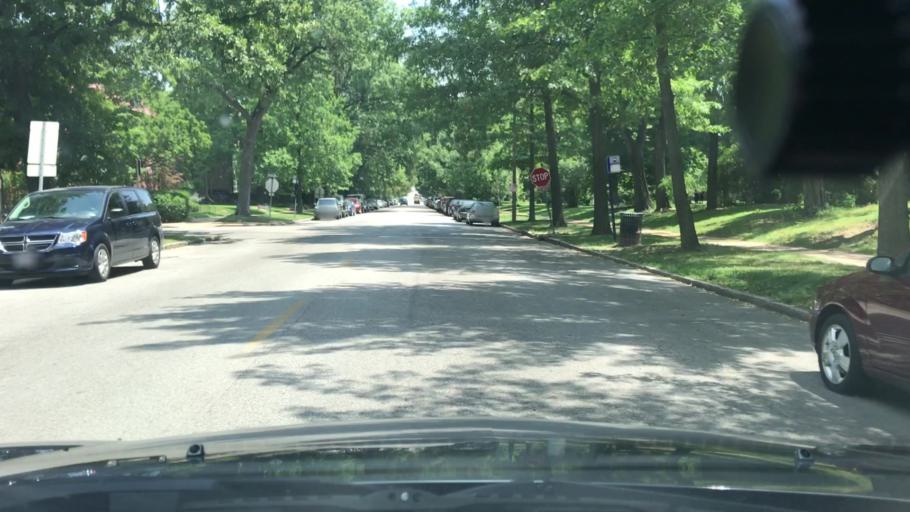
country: US
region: Missouri
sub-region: City of Saint Louis
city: St. Louis
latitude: 38.6085
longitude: -90.2552
